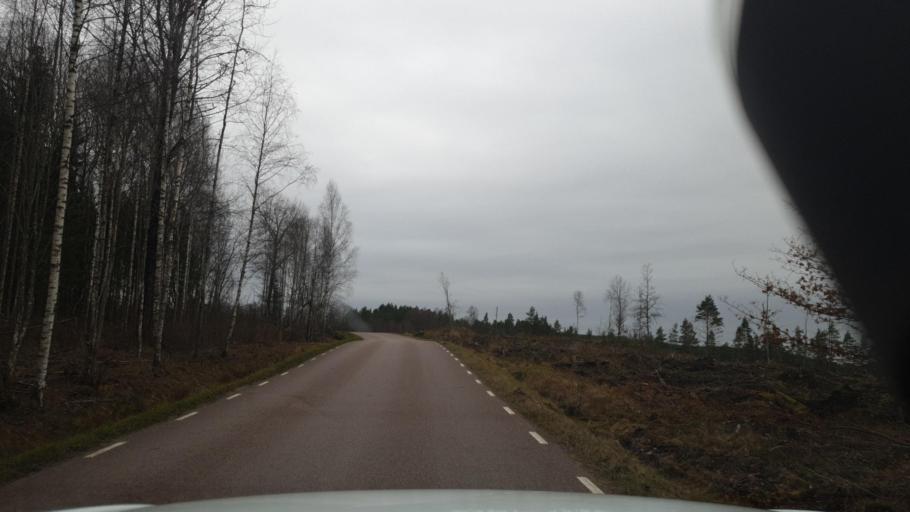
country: SE
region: Vaermland
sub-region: Grums Kommun
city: Grums
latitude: 59.4298
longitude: 13.0848
